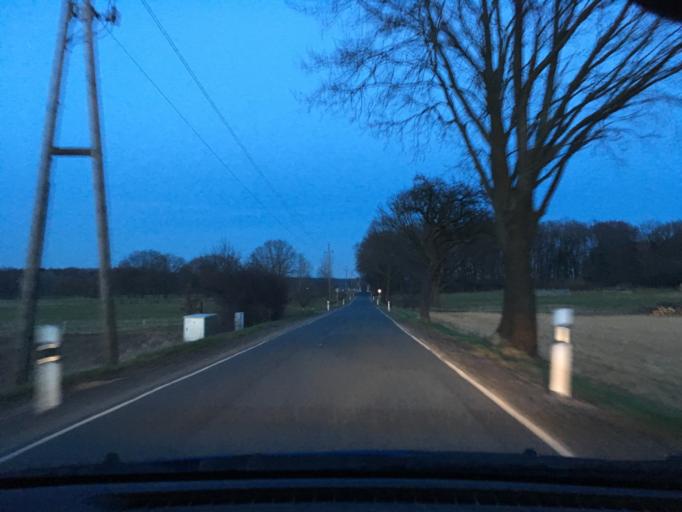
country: DE
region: Lower Saxony
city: Eyendorf
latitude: 53.2011
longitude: 10.1789
